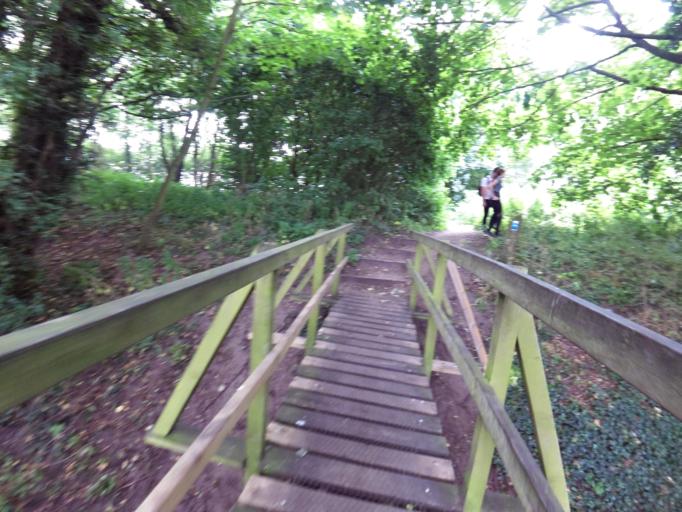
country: GB
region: England
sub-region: Norfolk
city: Diss
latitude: 52.3810
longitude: 1.1356
